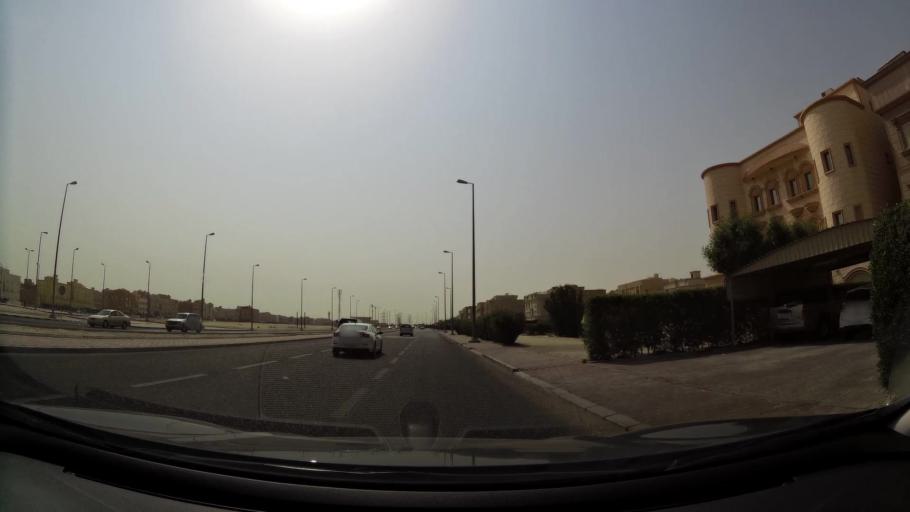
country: KW
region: Muhafazat al Jahra'
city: Al Jahra'
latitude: 29.3104
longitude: 47.7249
